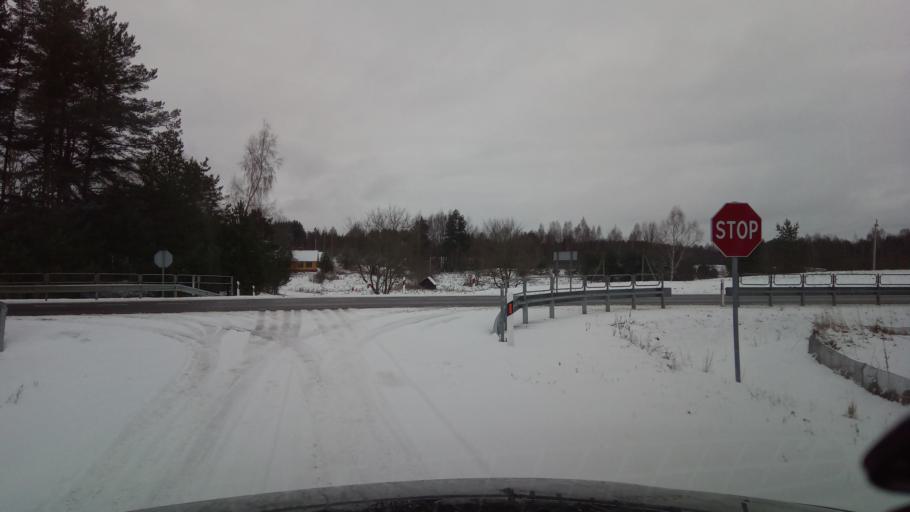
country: LT
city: Zarasai
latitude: 55.6717
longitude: 26.0924
